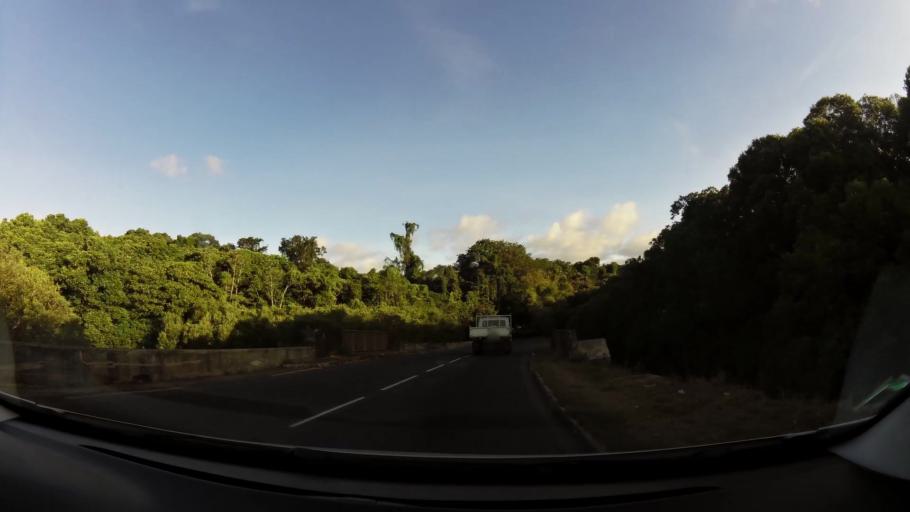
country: YT
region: Dembeni
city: Dembeni
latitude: -12.8303
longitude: 45.1930
